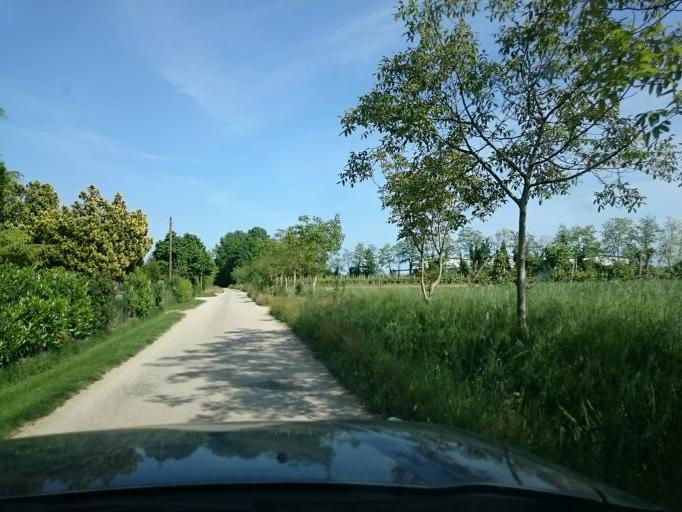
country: IT
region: Veneto
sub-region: Provincia di Venezia
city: Fornase
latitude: 45.4302
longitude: 12.1704
